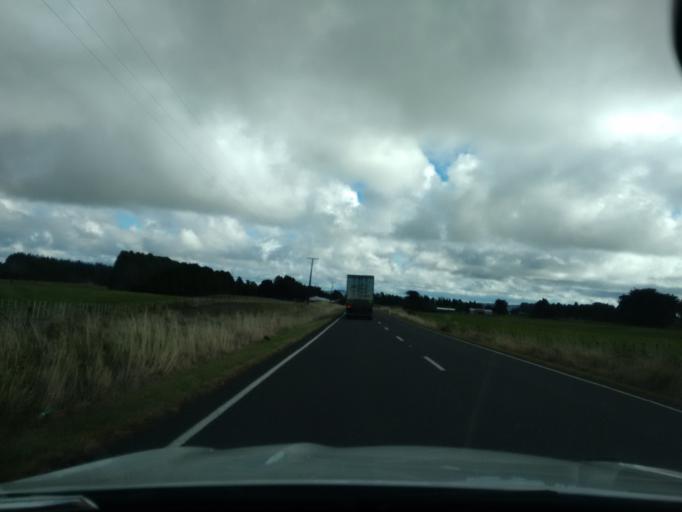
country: NZ
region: Manawatu-Wanganui
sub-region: Ruapehu District
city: Waiouru
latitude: -39.3572
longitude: 175.3519
